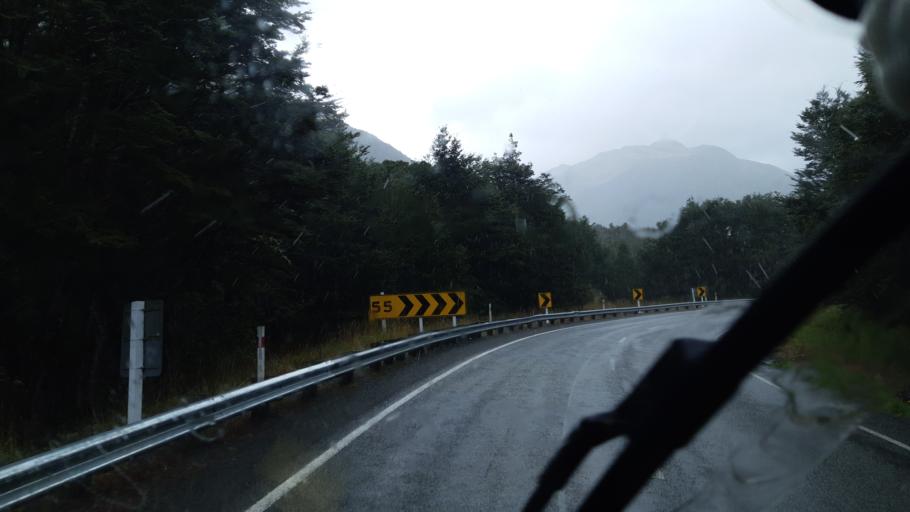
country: NZ
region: Canterbury
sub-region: Hurunui District
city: Amberley
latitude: -42.4309
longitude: 172.4027
